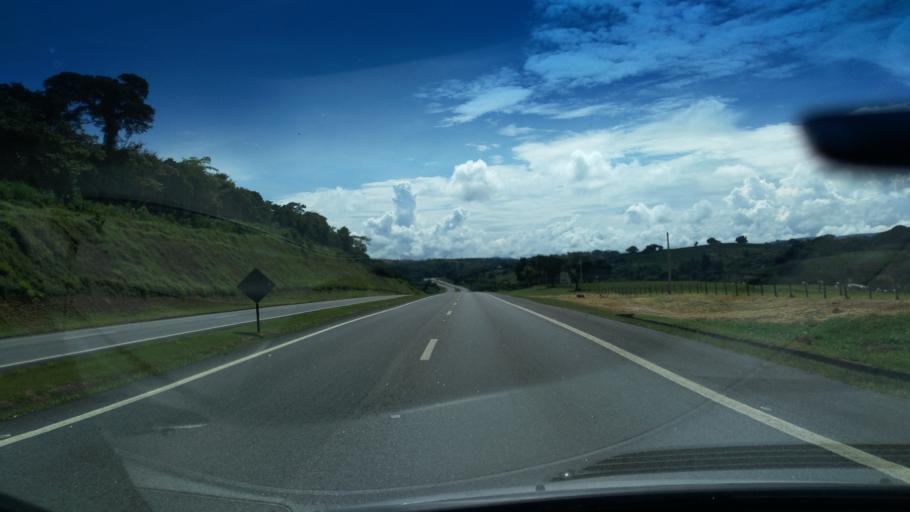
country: BR
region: Sao Paulo
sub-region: Santo Antonio Do Jardim
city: Espirito Santo do Pinhal
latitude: -22.2370
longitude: -46.7990
